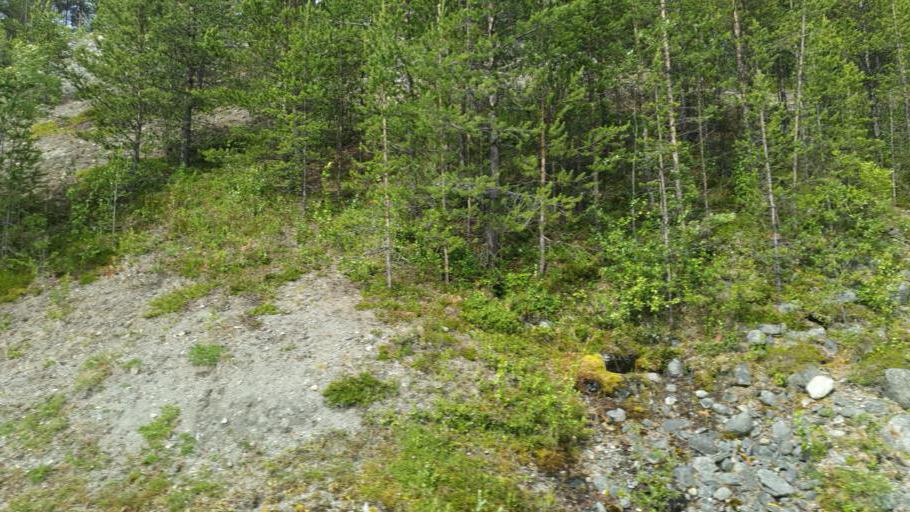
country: NO
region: Oppland
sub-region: Vaga
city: Vagamo
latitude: 61.6755
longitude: 9.0427
